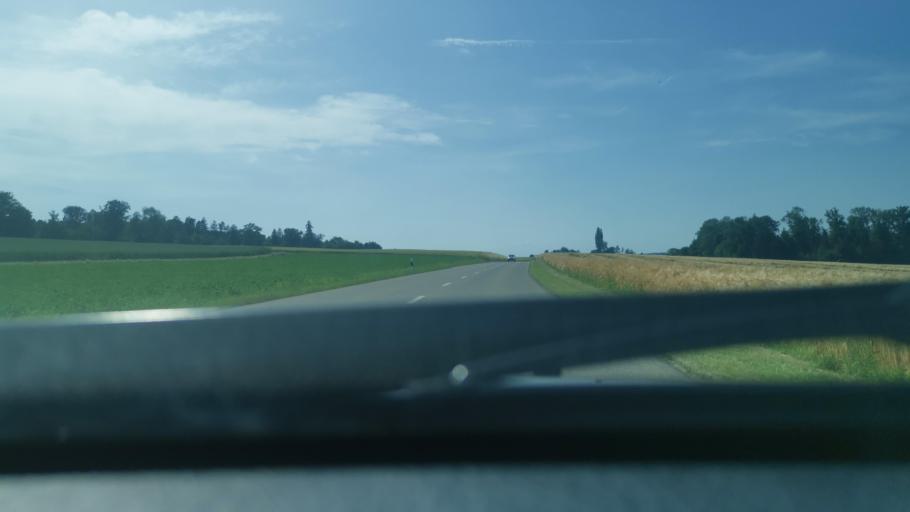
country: CH
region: Zurich
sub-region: Bezirk Winterthur
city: Sulz
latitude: 47.5635
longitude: 8.8156
